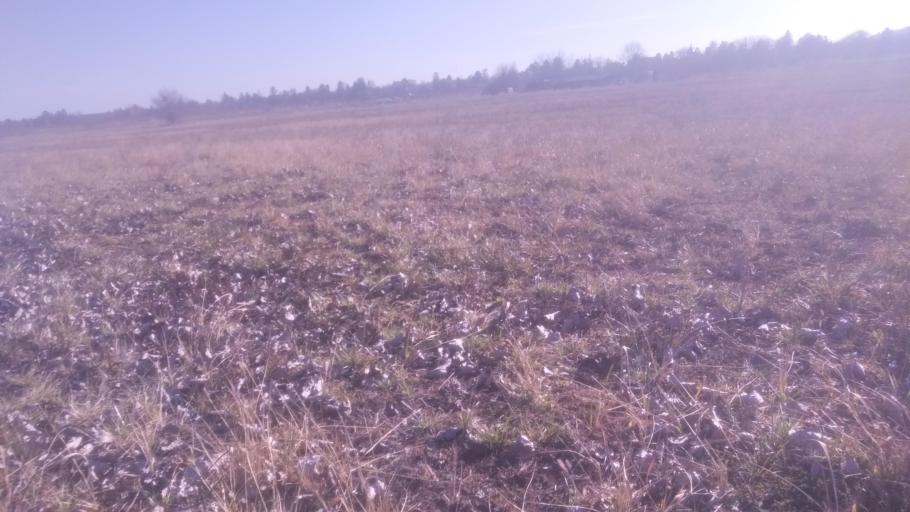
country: HU
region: Pest
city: Budakalasz
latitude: 47.6364
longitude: 19.0486
